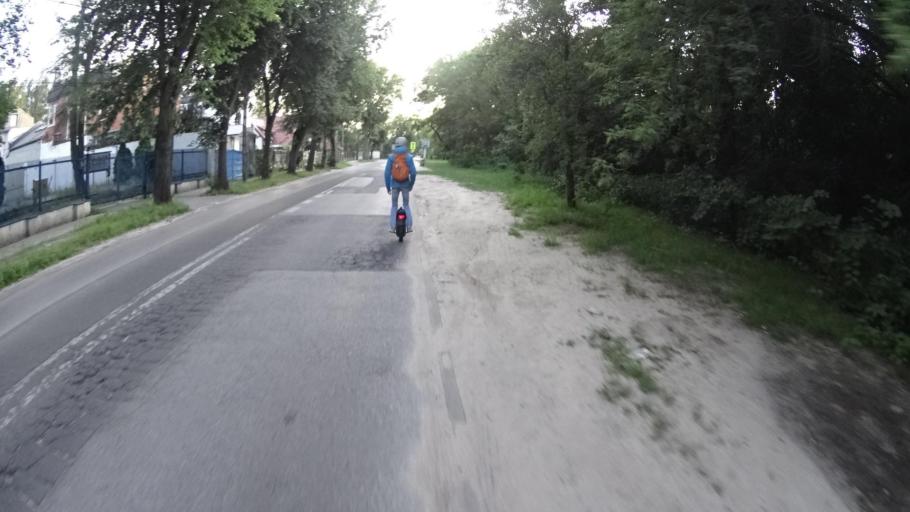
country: PL
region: Masovian Voivodeship
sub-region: Warszawa
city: Bielany
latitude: 52.3086
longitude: 20.9229
